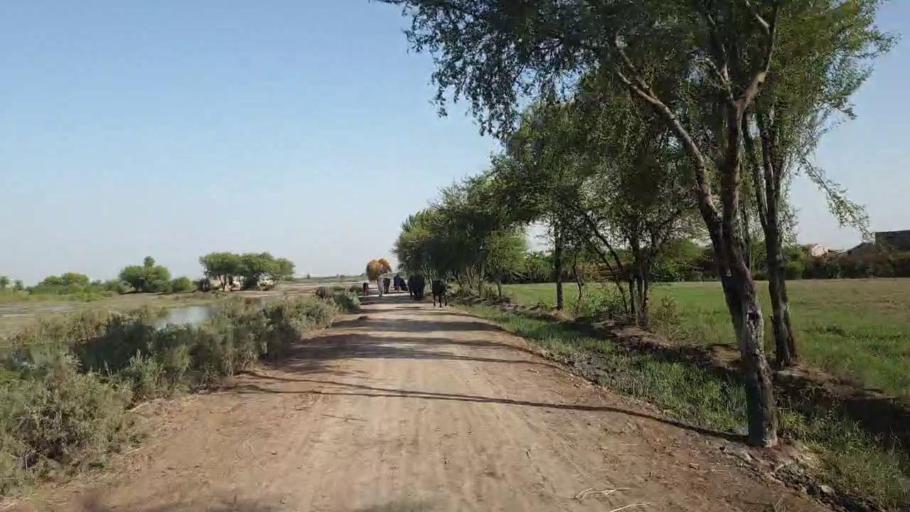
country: PK
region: Sindh
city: Badin
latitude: 24.5922
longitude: 68.9112
